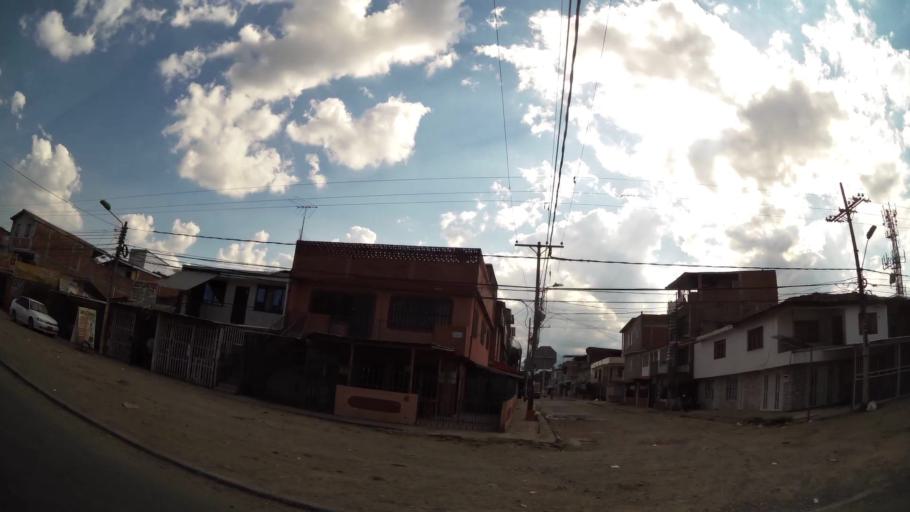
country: CO
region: Valle del Cauca
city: Cali
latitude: 3.4237
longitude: -76.5019
